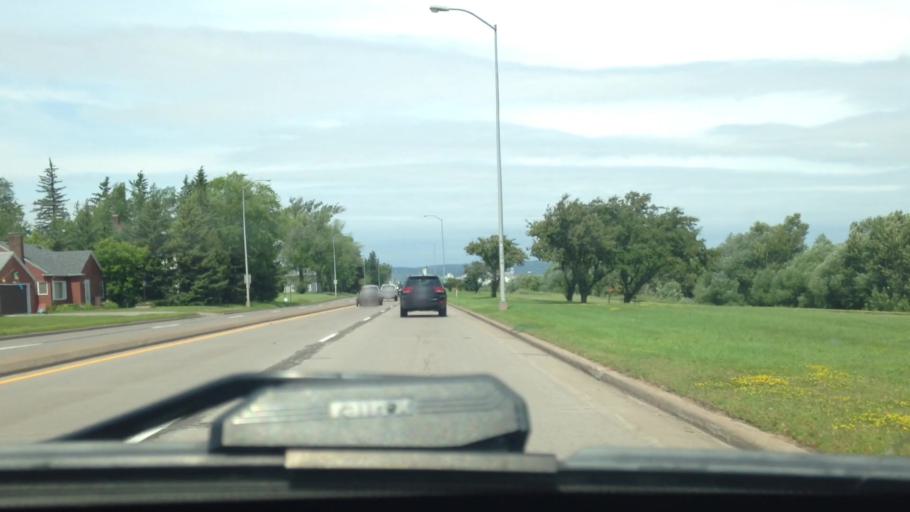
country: US
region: Wisconsin
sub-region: Douglas County
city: Superior
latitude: 46.7131
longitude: -92.0555
